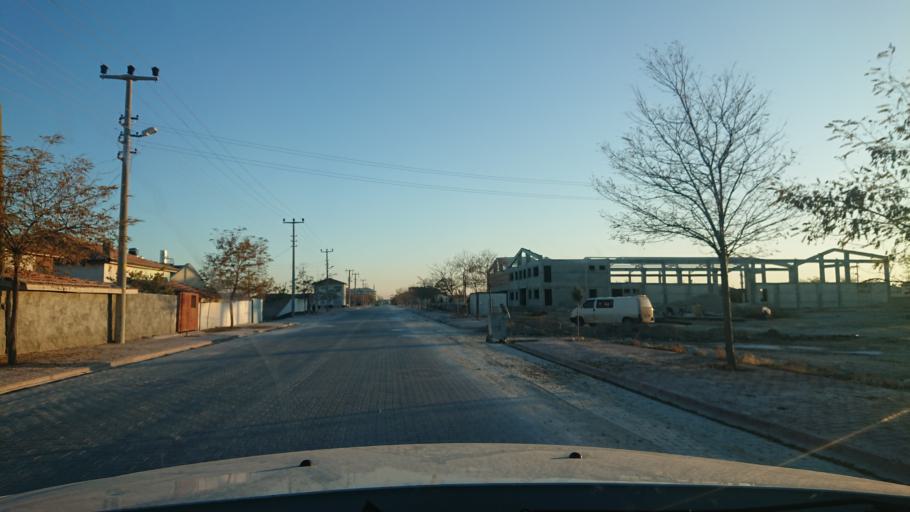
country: TR
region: Aksaray
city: Eskil
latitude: 38.3991
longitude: 33.4202
